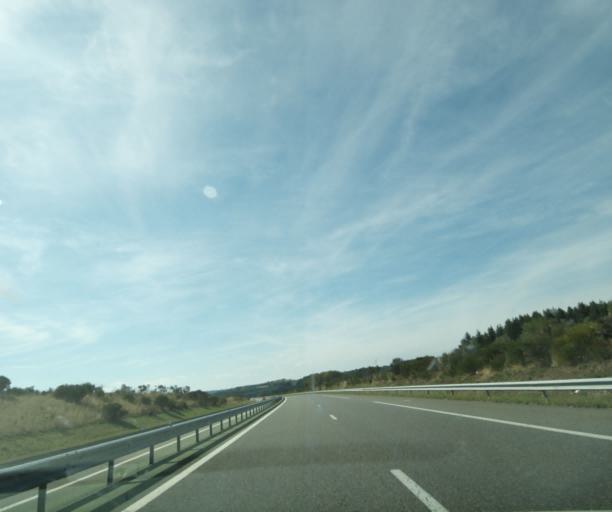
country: FR
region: Auvergne
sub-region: Departement du Puy-de-Dome
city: Saint-Ours
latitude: 45.8593
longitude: 2.8707
